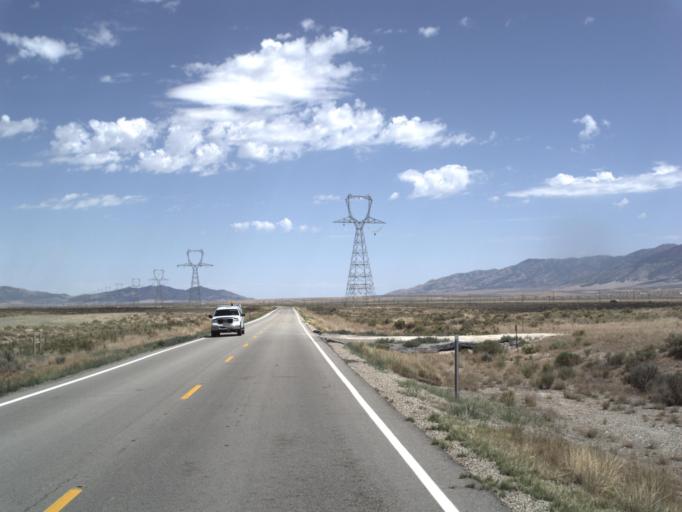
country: US
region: Utah
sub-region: Tooele County
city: Tooele
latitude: 40.2576
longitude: -112.3984
